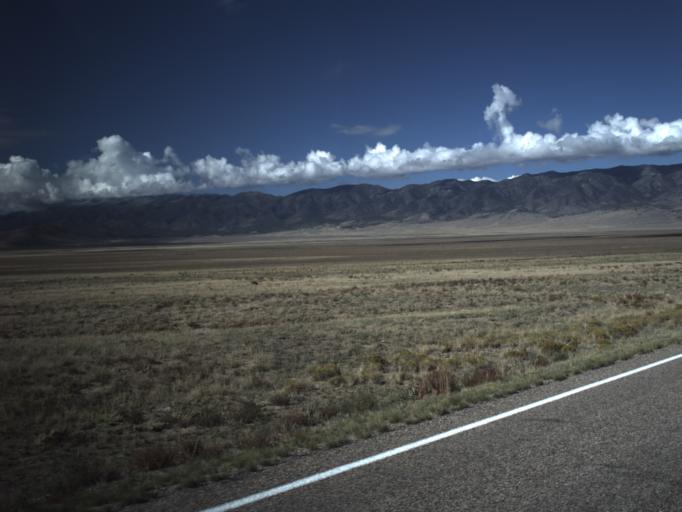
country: US
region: Utah
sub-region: Beaver County
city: Milford
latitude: 38.4551
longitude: -113.3595
